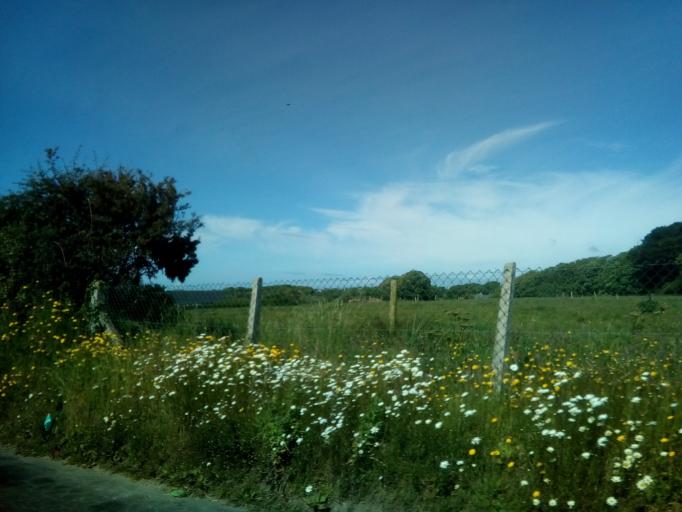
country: IE
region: Leinster
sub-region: Loch Garman
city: Loch Garman
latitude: 52.1960
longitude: -6.5577
